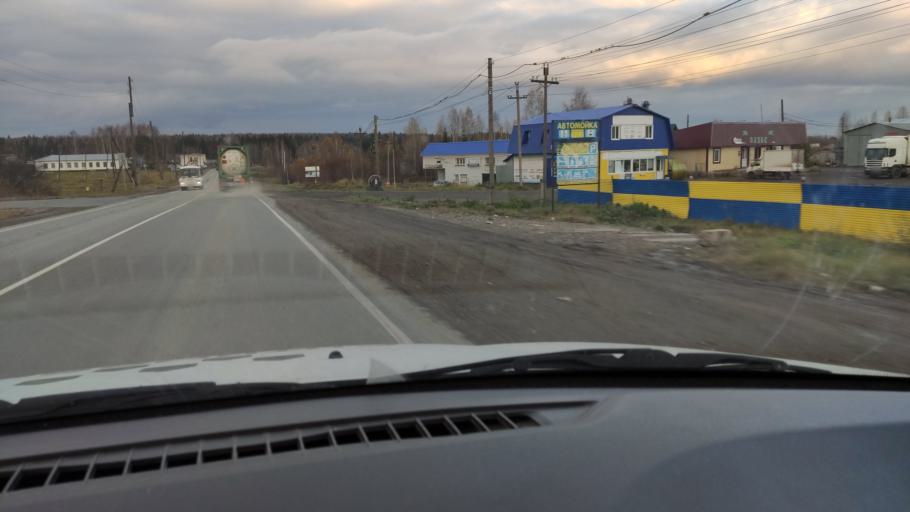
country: RU
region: Kirov
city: Omutninsk
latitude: 58.6949
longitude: 52.2197
